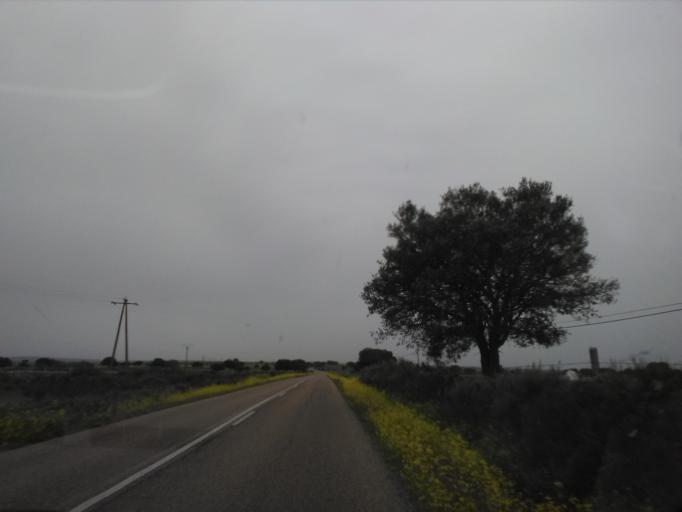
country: ES
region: Castille and Leon
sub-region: Provincia de Salamanca
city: Yecla de Yeltes
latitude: 40.9814
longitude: -6.4661
